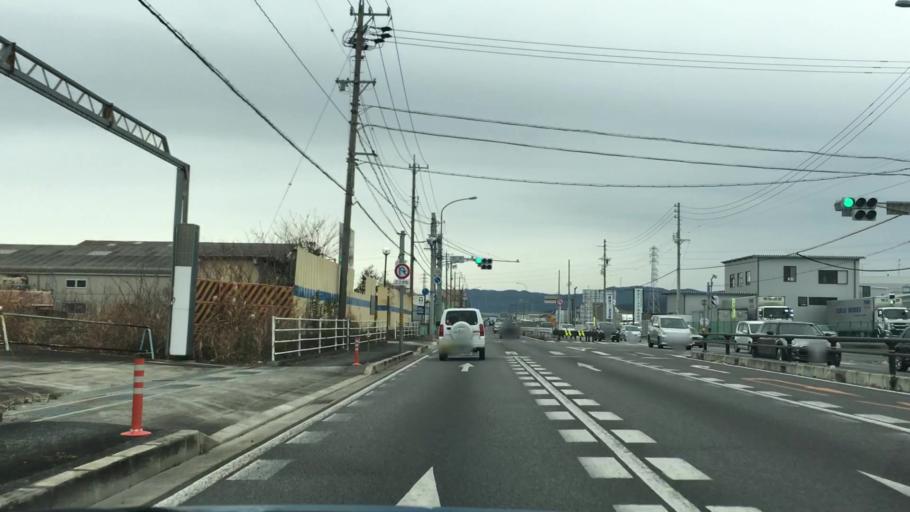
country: JP
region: Aichi
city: Kozakai-cho
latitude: 34.8214
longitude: 137.3451
